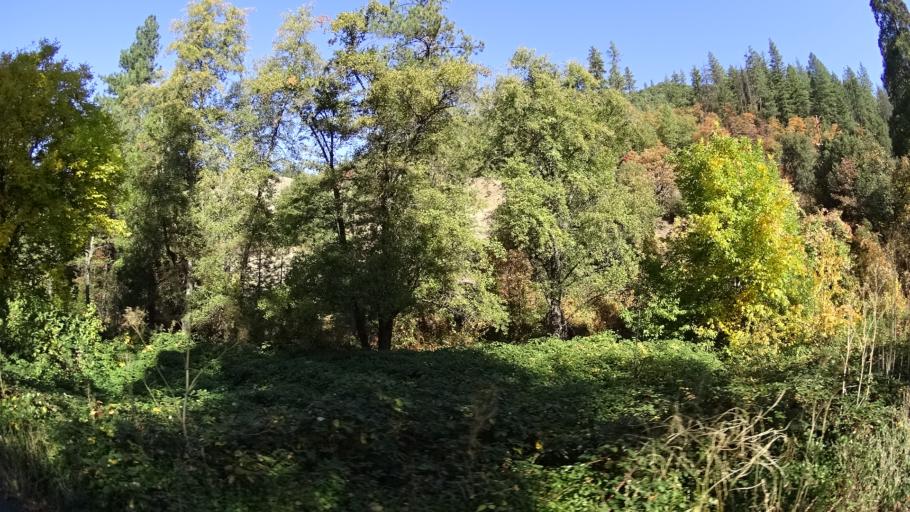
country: US
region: California
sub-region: Siskiyou County
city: Yreka
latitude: 41.7417
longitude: -122.9961
